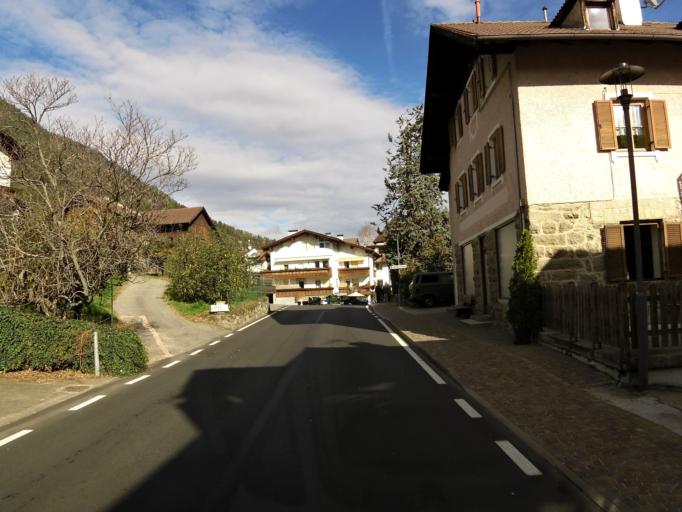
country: IT
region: Trentino-Alto Adige
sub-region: Bolzano
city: Rifiano
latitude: 46.7007
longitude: 11.1793
